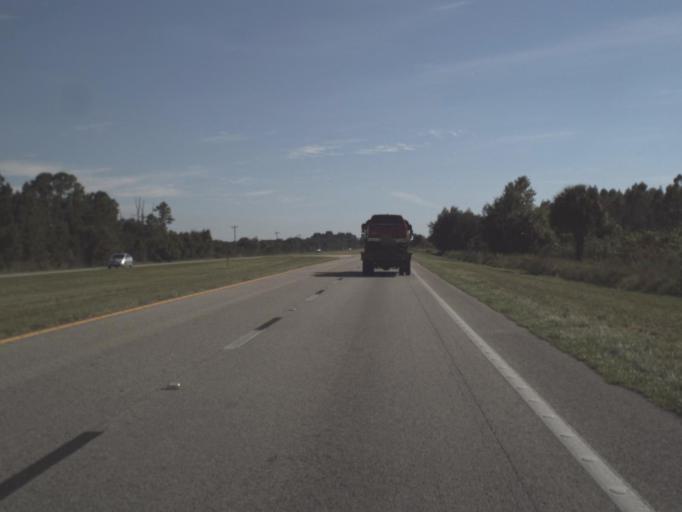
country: US
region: Florida
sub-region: Hendry County
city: Port LaBelle
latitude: 26.9810
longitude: -81.3214
